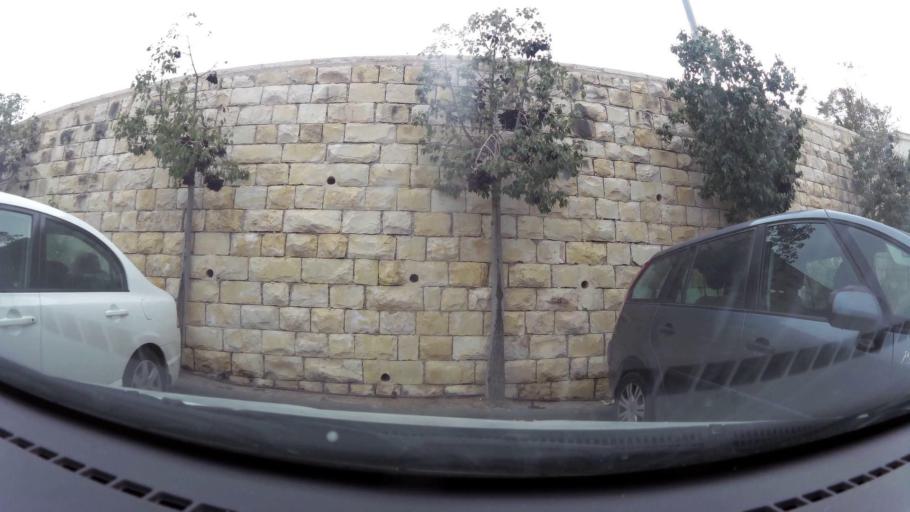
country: IL
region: Jerusalem
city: Bet Shemesh
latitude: 31.7148
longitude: 34.9944
